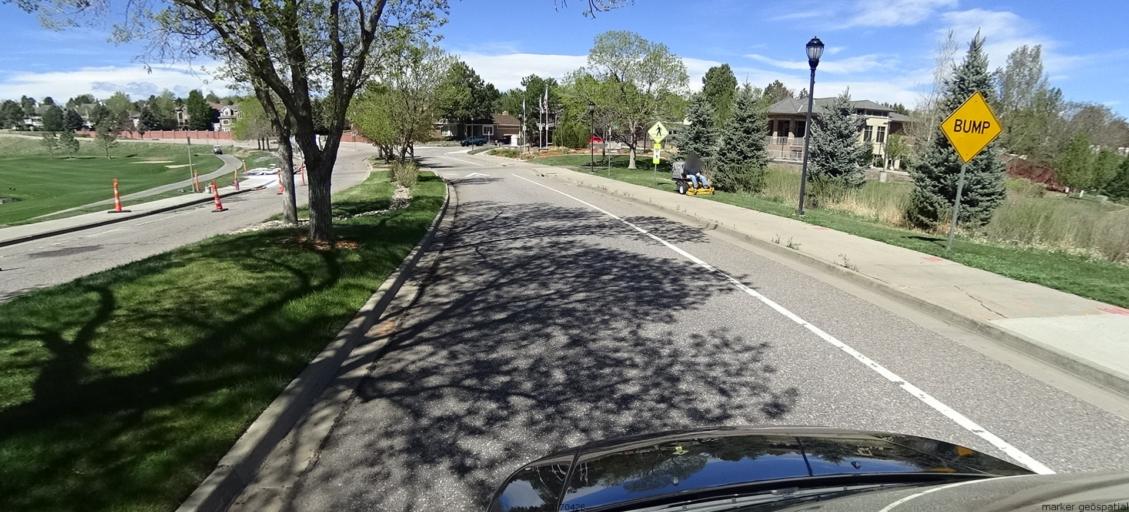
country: US
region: Colorado
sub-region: Adams County
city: Lone Tree
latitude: 39.5479
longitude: -104.8889
